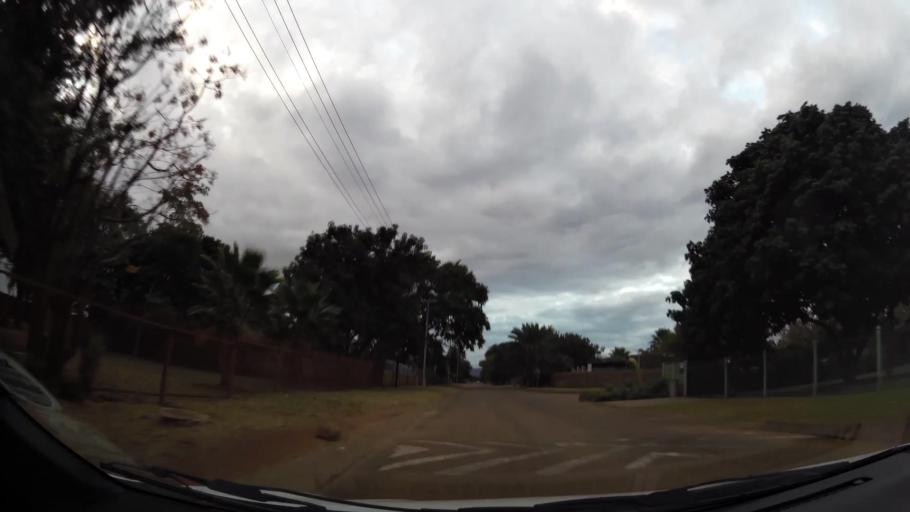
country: ZA
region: Limpopo
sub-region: Waterberg District Municipality
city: Mokopane
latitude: -24.1877
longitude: 28.9906
